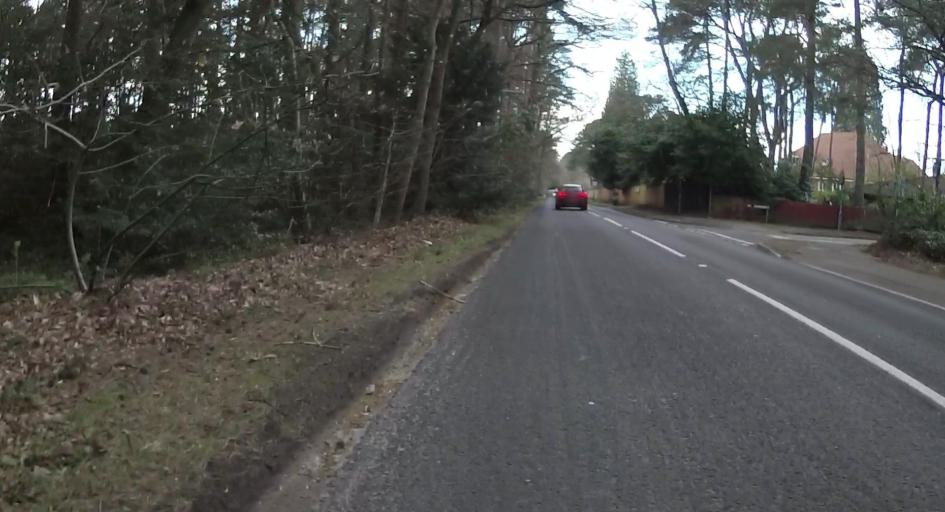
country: GB
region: England
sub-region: Surrey
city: Bagshot
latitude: 51.3230
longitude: -0.7020
